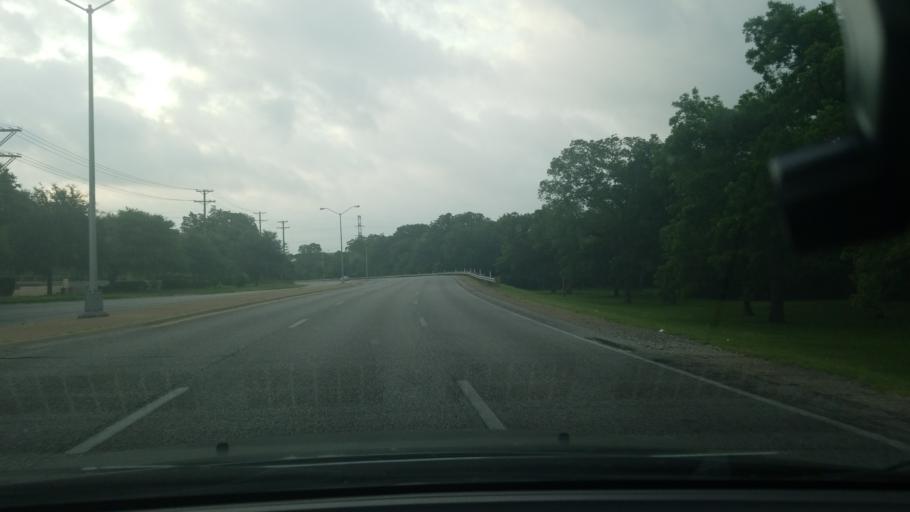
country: US
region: Texas
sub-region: Dallas County
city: Balch Springs
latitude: 32.7633
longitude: -96.6927
